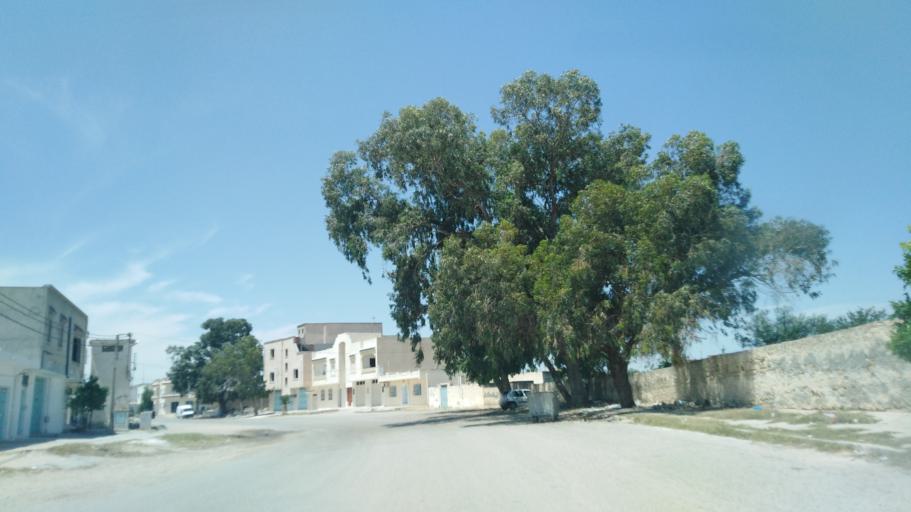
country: TN
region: Al Mahdiyah
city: Ksour Essaf
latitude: 35.4161
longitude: 10.9804
